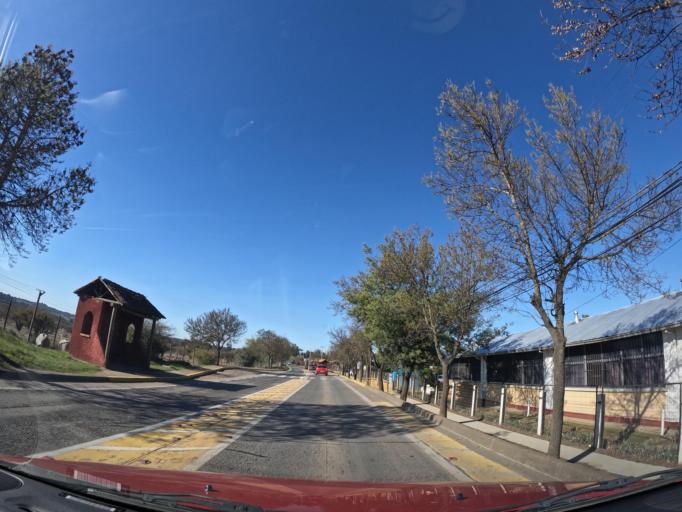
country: CL
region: Maule
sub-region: Provincia de Cauquenes
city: Cauquenes
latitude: -35.9578
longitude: -72.2992
